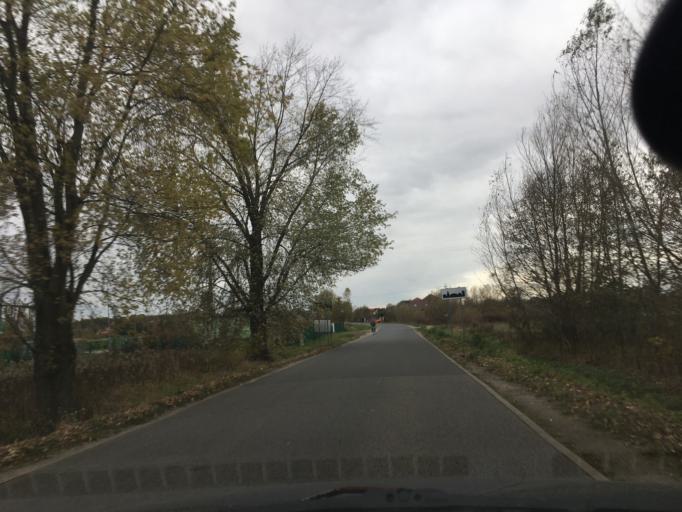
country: PL
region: Lodz Voivodeship
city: Zabia Wola
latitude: 52.0277
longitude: 20.7007
